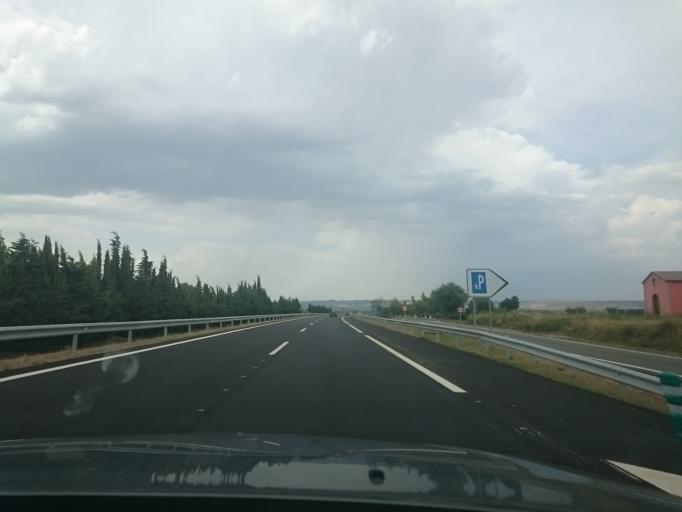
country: ES
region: La Rioja
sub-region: Provincia de La Rioja
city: Aldeanueva de Ebro
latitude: 42.2349
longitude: -1.9011
